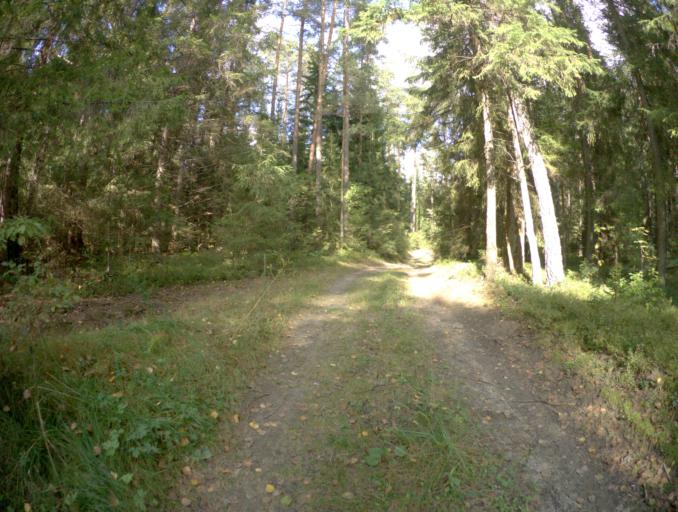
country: RU
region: Vladimir
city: Kommunar
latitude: 56.0283
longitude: 40.5221
